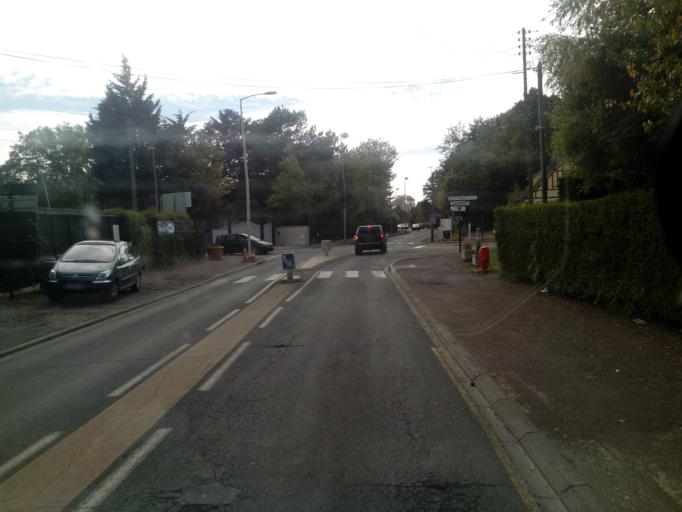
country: FR
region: Lower Normandy
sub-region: Departement du Calvados
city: Cabourg
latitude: 49.2856
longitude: -0.1388
